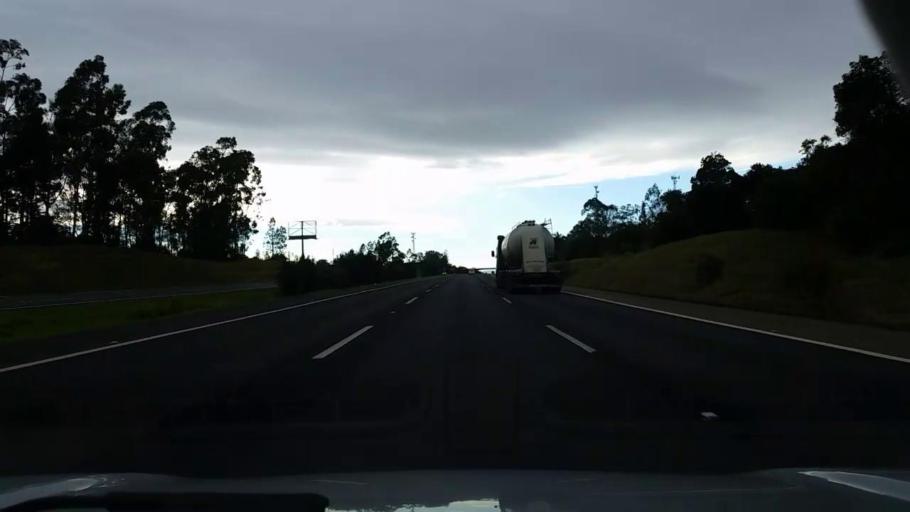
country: BR
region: Rio Grande do Sul
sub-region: Taquara
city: Taquara
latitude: -29.8906
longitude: -50.7120
